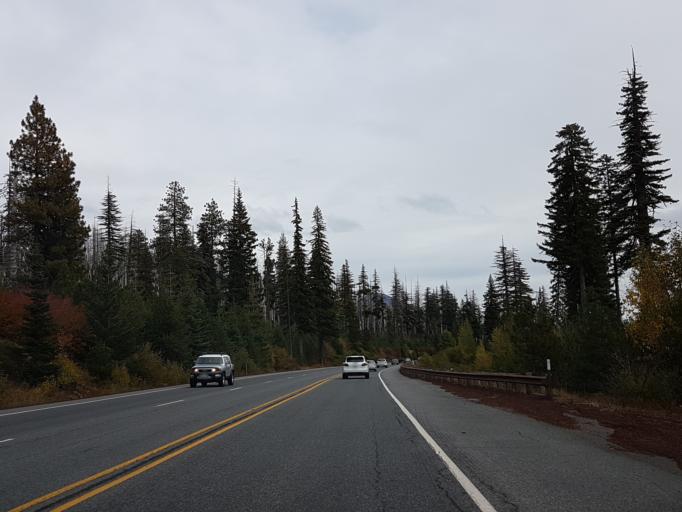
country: US
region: Oregon
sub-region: Deschutes County
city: Sisters
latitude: 44.4236
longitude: -121.7980
